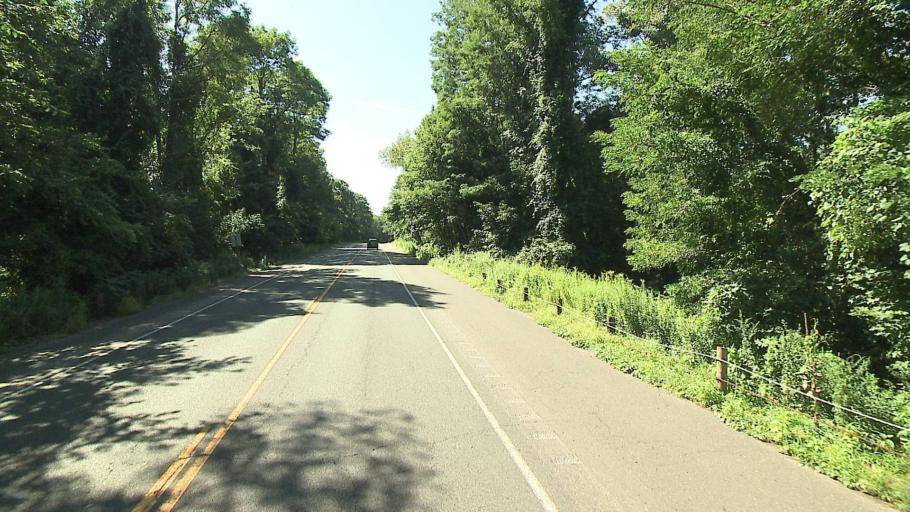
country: US
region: Connecticut
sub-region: Hartford County
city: Tariffville
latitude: 41.9039
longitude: -72.7472
